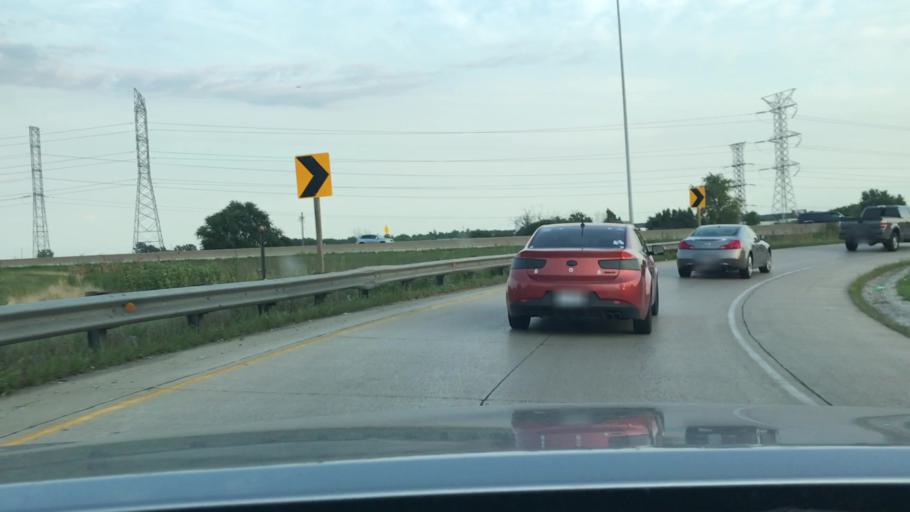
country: US
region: Illinois
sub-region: Cook County
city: Hodgkins
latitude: 41.7630
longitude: -87.8657
